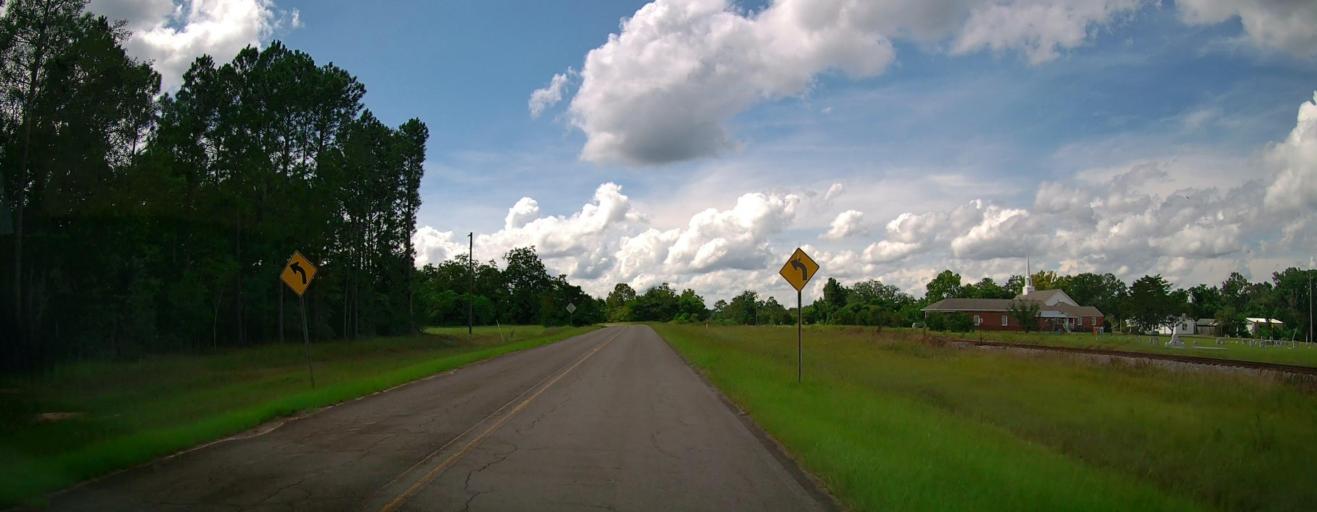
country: US
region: Georgia
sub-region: Taylor County
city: Butler
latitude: 32.5956
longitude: -84.3800
